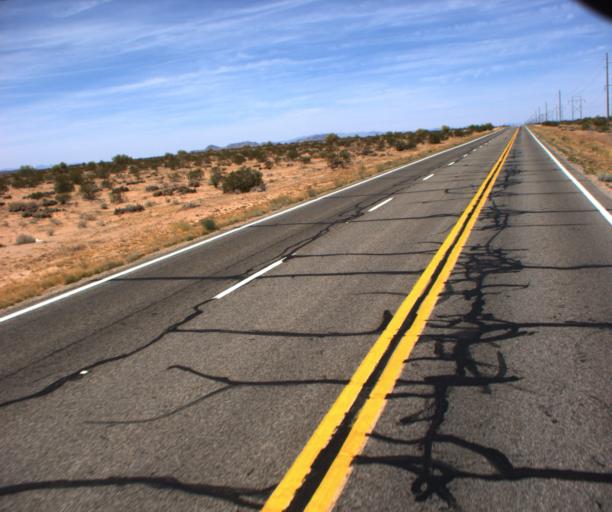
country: US
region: Arizona
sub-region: La Paz County
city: Quartzsite
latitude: 33.8131
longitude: -114.2170
